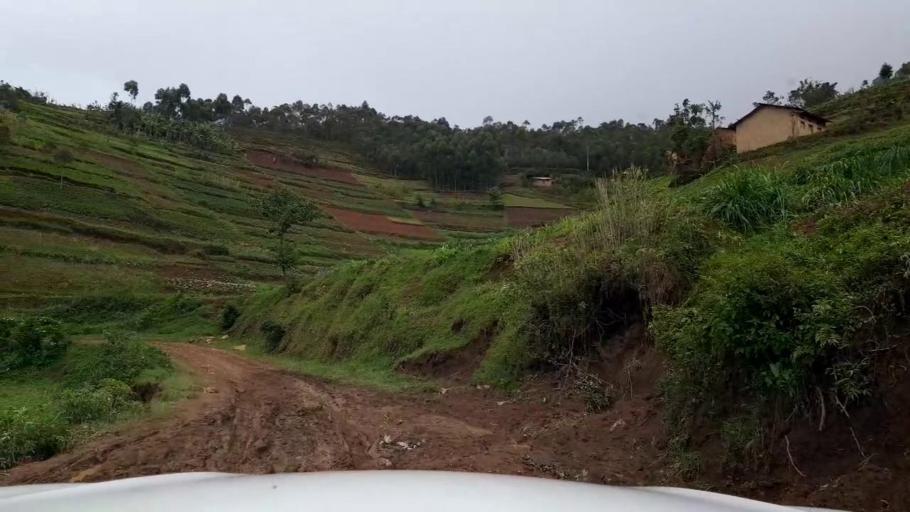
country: RW
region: Northern Province
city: Musanze
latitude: -1.6015
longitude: 29.7682
